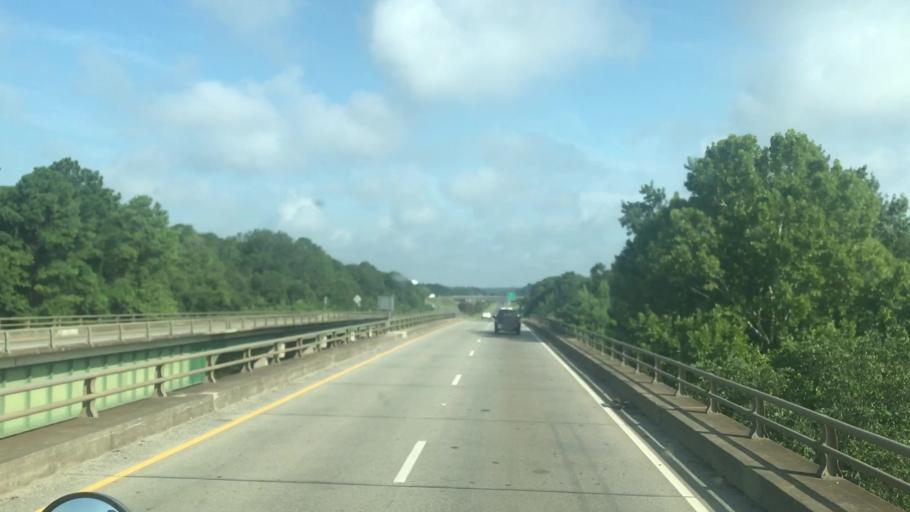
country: US
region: Georgia
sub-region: Decatur County
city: Bainbridge
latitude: 30.9065
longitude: -84.5888
